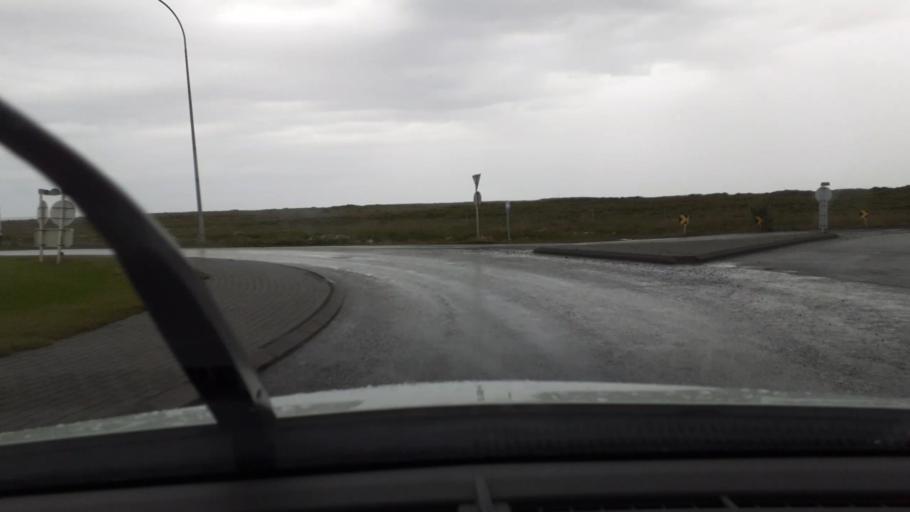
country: IS
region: West
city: Akranes
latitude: 64.3277
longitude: -22.0525
